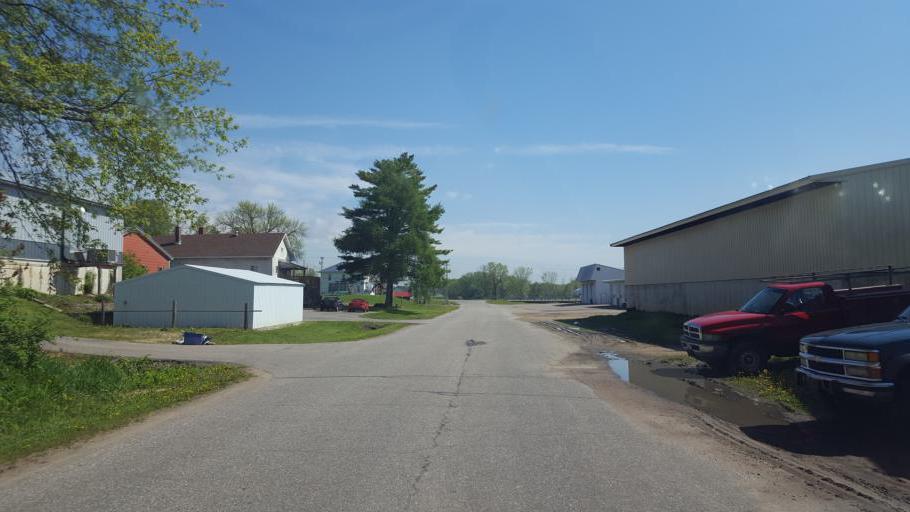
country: US
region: Wisconsin
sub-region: Vernon County
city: Hillsboro
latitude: 43.6517
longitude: -90.3378
